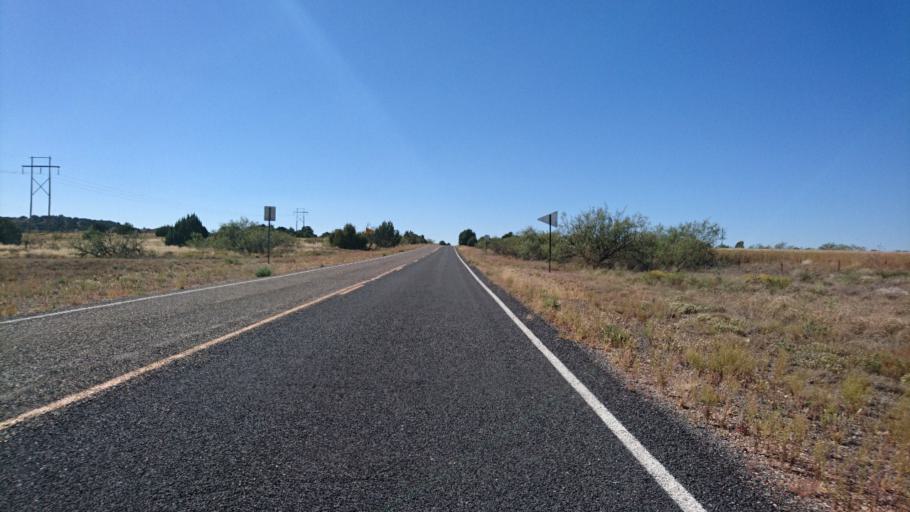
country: US
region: New Mexico
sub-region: Quay County
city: Tucumcari
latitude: 35.0687
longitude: -104.1681
